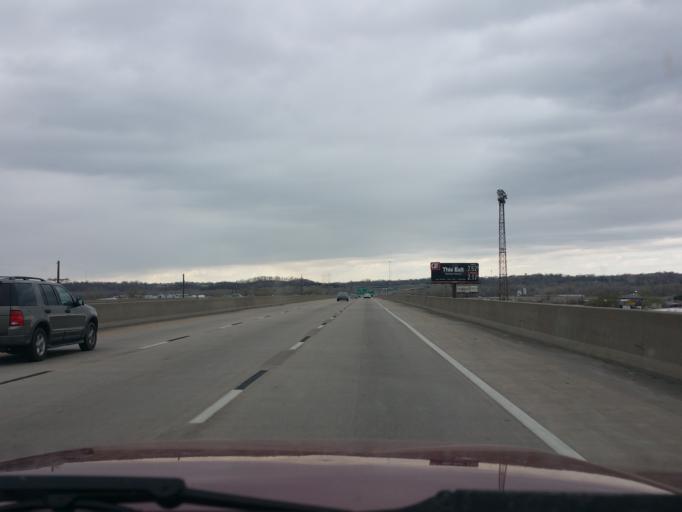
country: US
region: Kansas
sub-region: Johnson County
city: Shawnee
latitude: 39.0852
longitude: -94.6804
